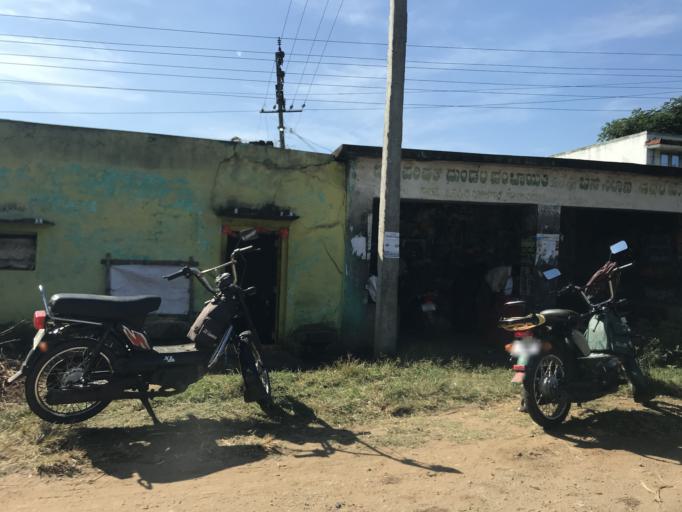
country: IN
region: Karnataka
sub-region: Mysore
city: Heggadadevankote
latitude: 12.1258
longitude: 76.4573
